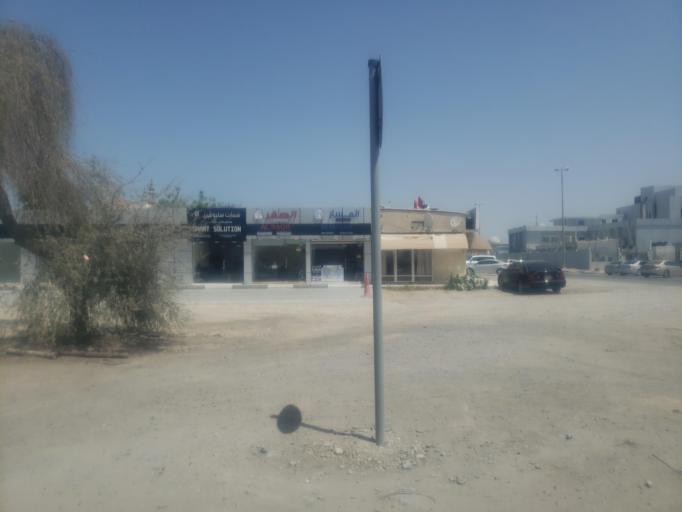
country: AE
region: Ra's al Khaymah
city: Ras al-Khaimah
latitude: 25.8026
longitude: 55.9717
